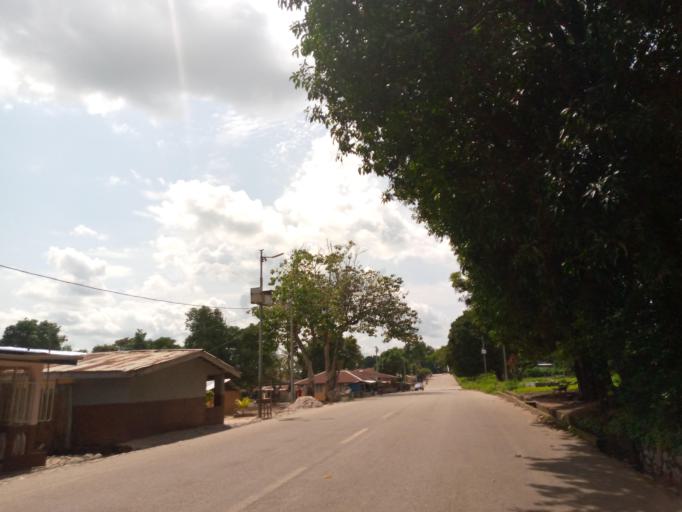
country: SL
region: Northern Province
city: Magburaka
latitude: 8.7173
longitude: -11.9377
